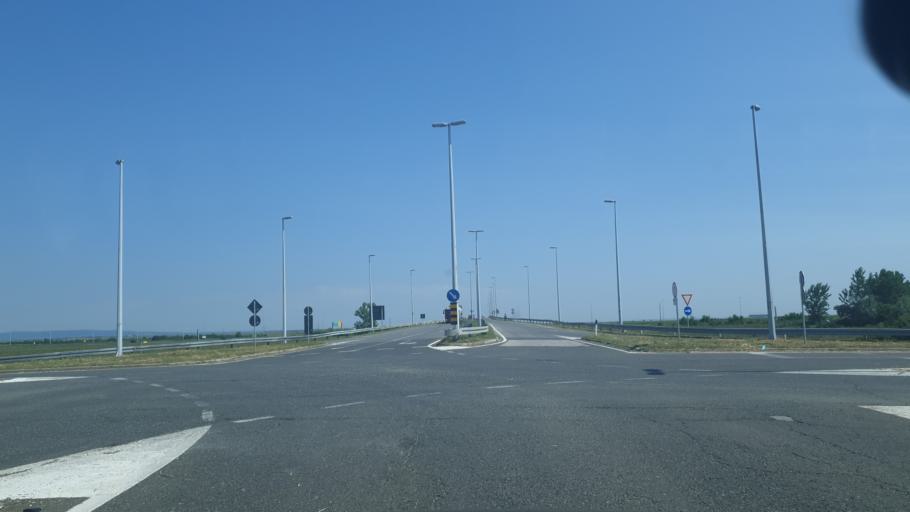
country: RS
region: Autonomna Pokrajina Vojvodina
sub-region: Sremski Okrug
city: Pecinci
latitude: 44.9173
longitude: 19.9574
